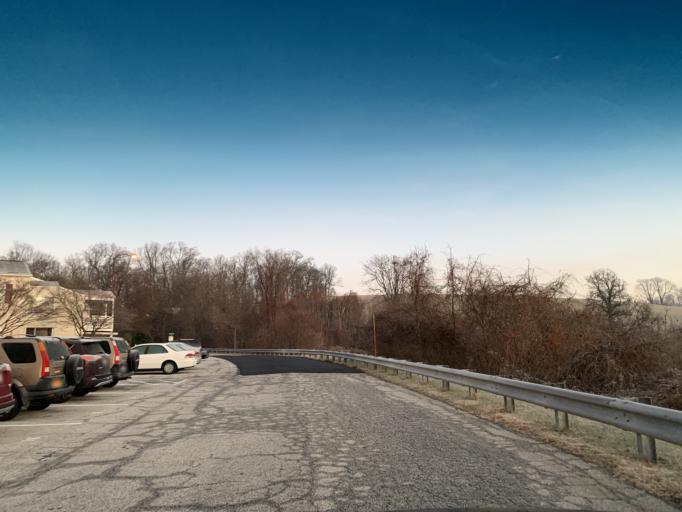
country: US
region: Maryland
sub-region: Baltimore County
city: Carney
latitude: 39.4481
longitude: -76.5158
